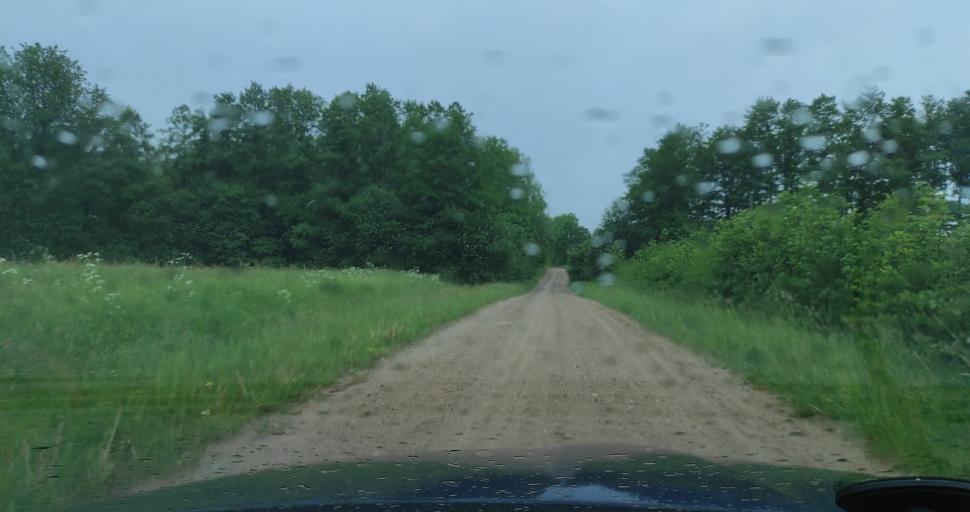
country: LV
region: Alsunga
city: Alsunga
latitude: 56.9891
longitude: 21.3934
